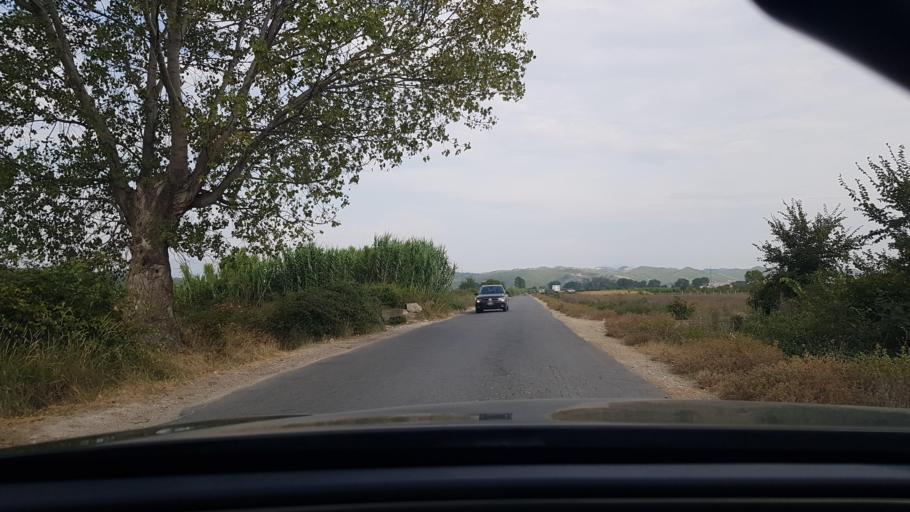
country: AL
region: Durres
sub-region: Rrethi i Durresit
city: Katundi i Ri
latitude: 41.4841
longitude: 19.5309
